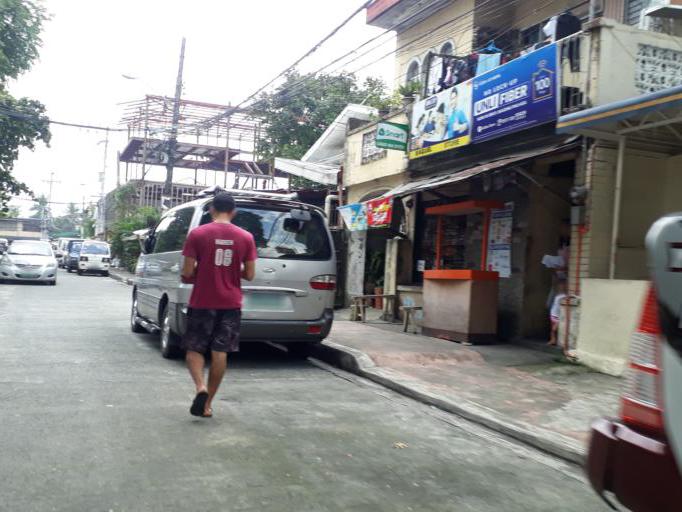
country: PH
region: Calabarzon
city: Bagong Pagasa
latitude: 14.6623
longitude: 121.0334
